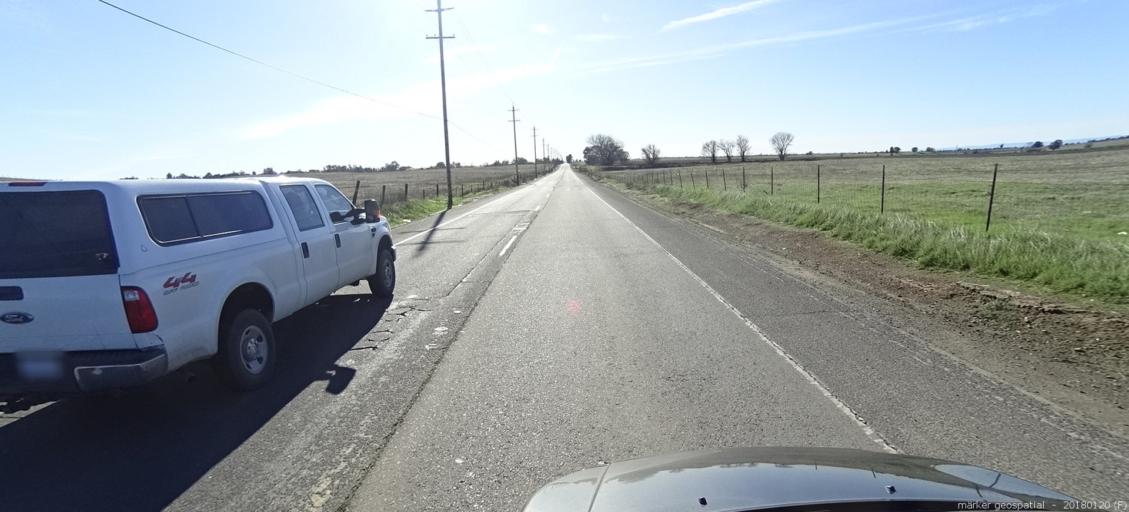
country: US
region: California
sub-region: Sacramento County
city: Rancho Murieta
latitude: 38.5140
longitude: -121.2098
